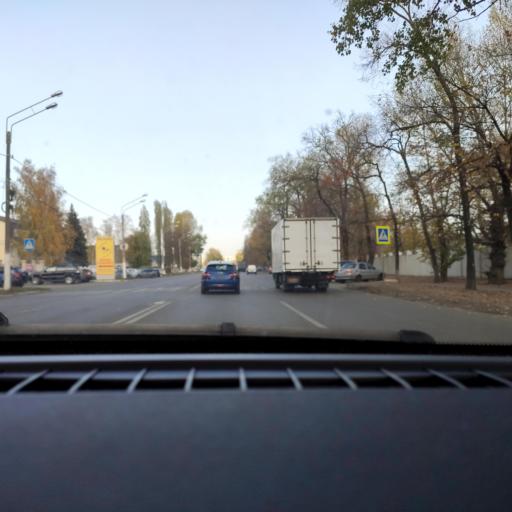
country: RU
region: Voronezj
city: Voronezh
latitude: 51.6485
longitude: 39.2682
